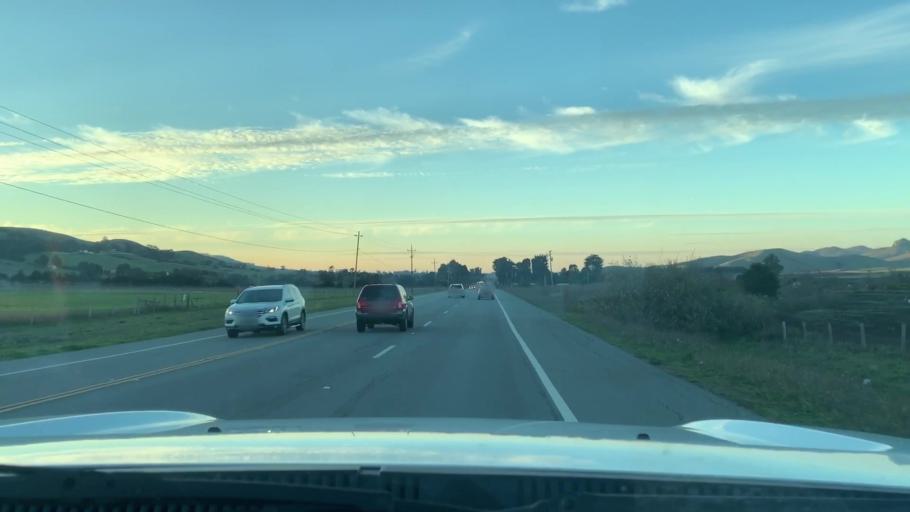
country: US
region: California
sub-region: San Luis Obispo County
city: Los Osos
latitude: 35.2899
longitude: -120.7474
